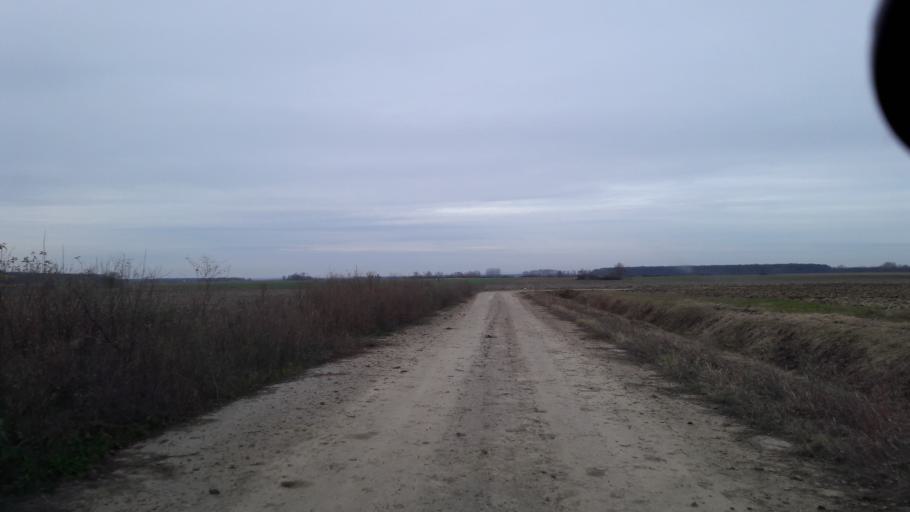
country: HR
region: Osjecko-Baranjska
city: Vladislavci
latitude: 45.4265
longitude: 18.5750
